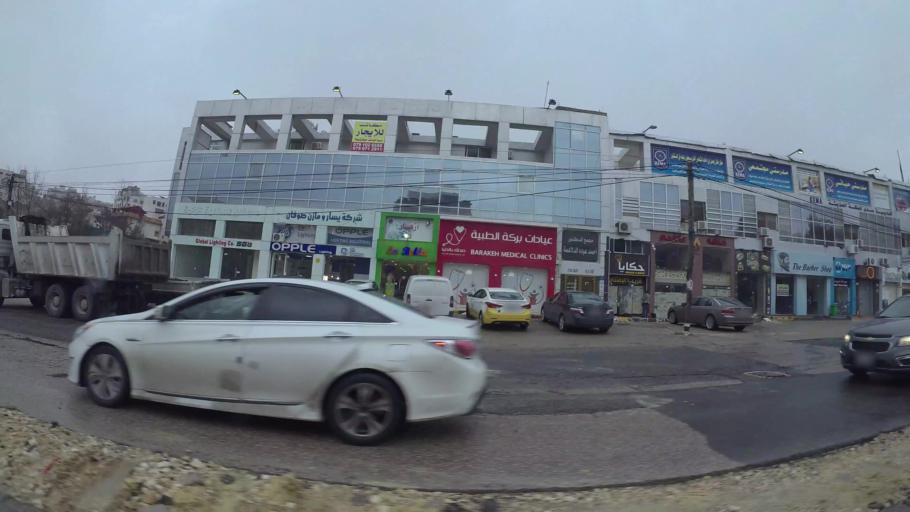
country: JO
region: Amman
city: Al Jubayhah
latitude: 32.0155
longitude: 35.8339
